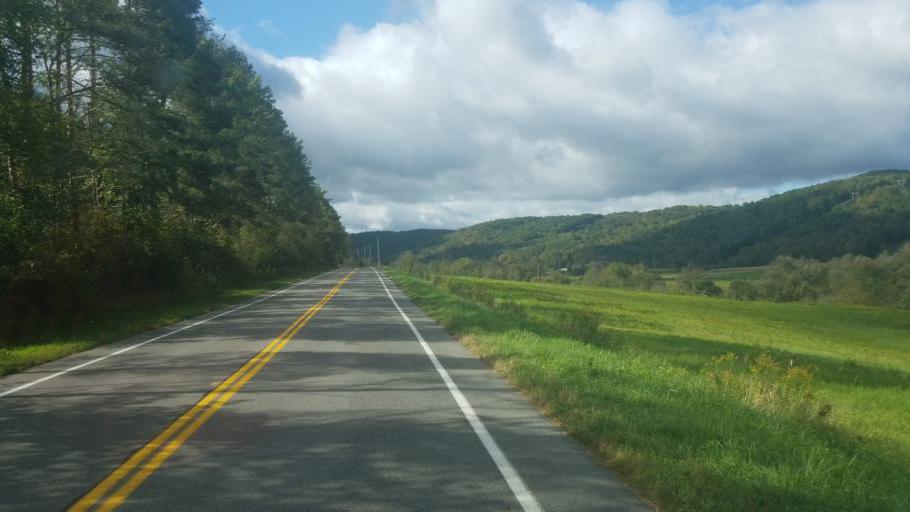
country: US
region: New York
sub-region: Cattaraugus County
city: Weston Mills
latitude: 42.1330
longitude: -78.3379
